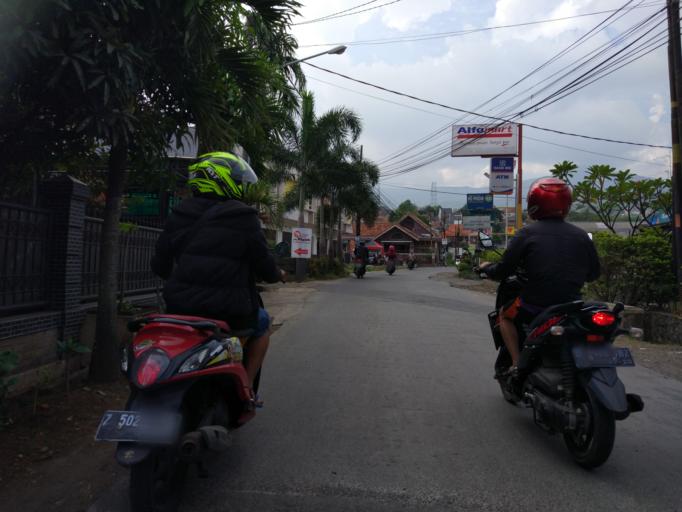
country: ID
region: West Java
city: Cileunyi
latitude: -6.9021
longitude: 107.6912
